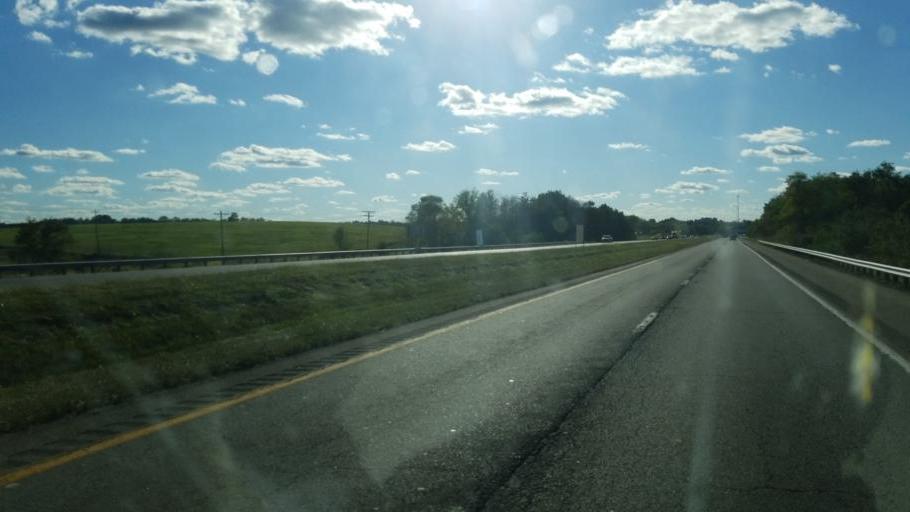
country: US
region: Ohio
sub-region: Belmont County
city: Saint Clairsville
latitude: 40.0646
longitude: -80.9914
